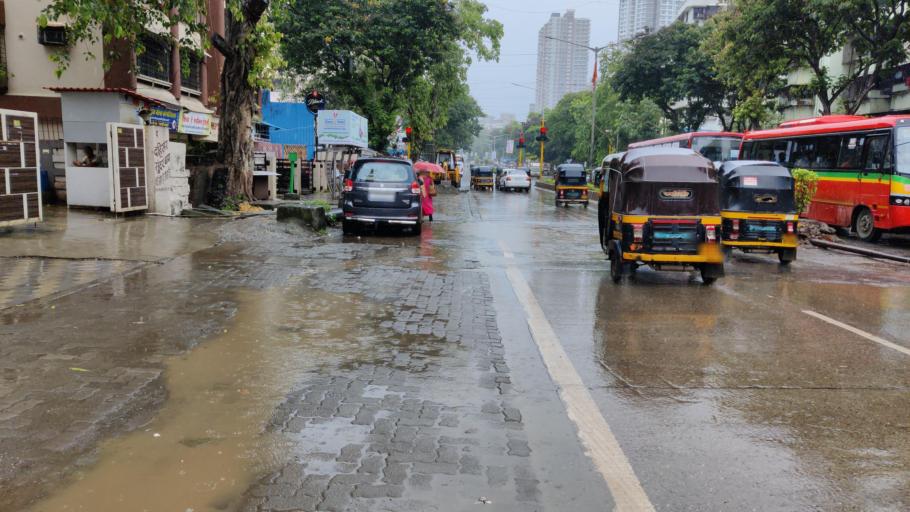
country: IN
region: Maharashtra
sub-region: Mumbai Suburban
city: Borivli
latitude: 19.2455
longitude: 72.8607
